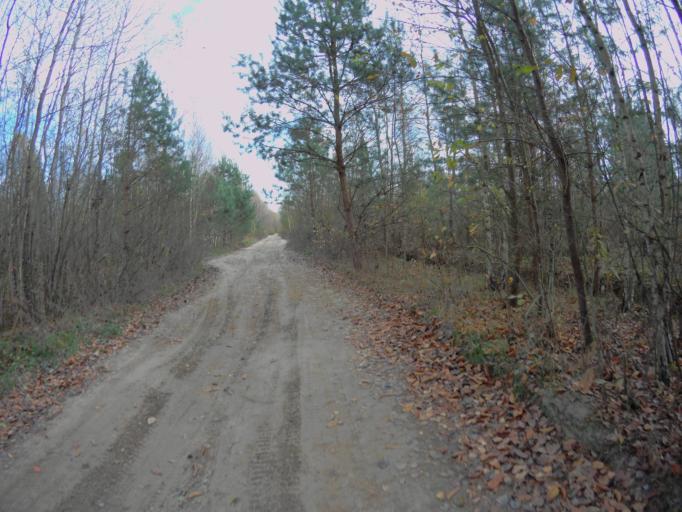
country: PL
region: Subcarpathian Voivodeship
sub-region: Powiat kolbuszowski
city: Lipnica
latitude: 50.3247
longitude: 21.9396
